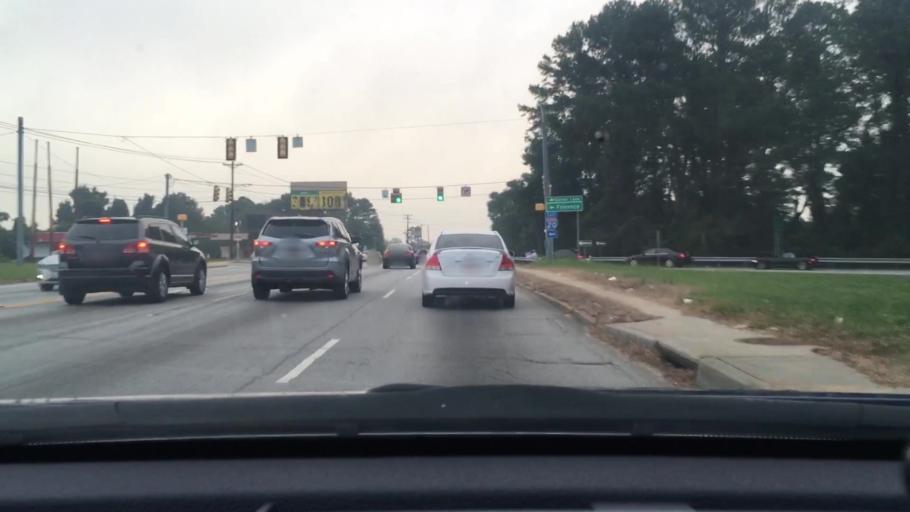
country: US
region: South Carolina
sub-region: Lexington County
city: Saint Andrews
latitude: 34.0391
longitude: -81.0935
